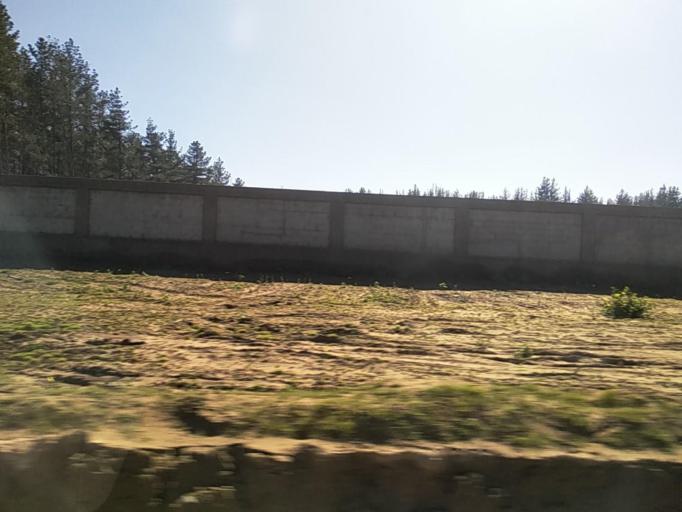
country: CL
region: Valparaiso
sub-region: Provincia de Valparaiso
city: Vina del Mar
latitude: -32.9581
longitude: -71.5263
